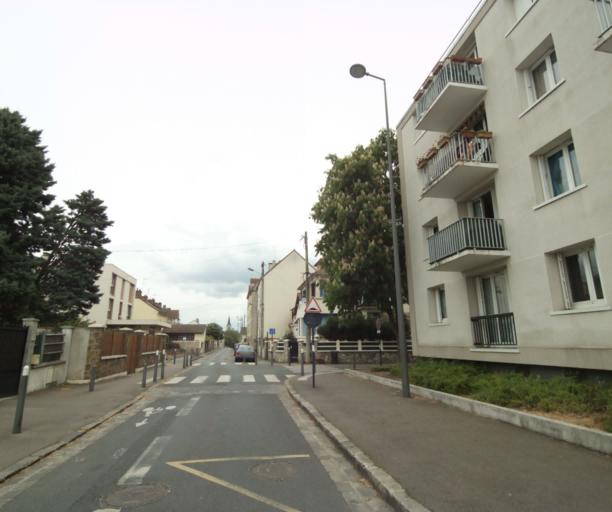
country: FR
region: Ile-de-France
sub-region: Departement des Yvelines
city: Les Mureaux
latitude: 48.9886
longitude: 1.9093
